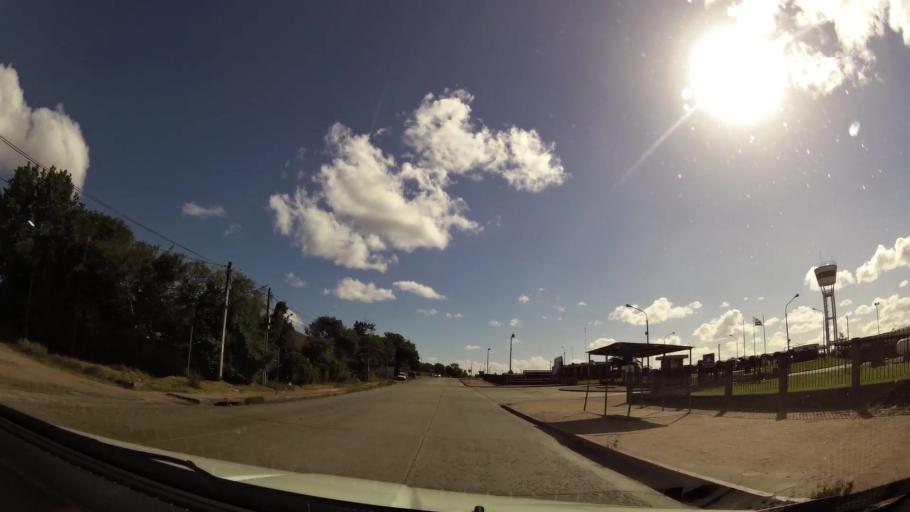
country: UY
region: Canelones
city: La Paz
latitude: -34.8209
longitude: -56.2386
